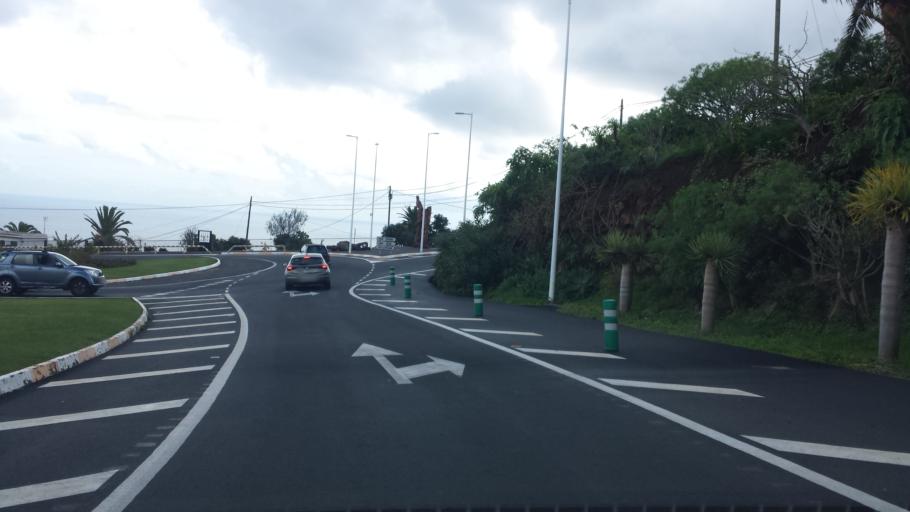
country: ES
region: Canary Islands
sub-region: Provincia de Santa Cruz de Tenerife
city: Brena Alta
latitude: 28.6612
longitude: -17.7814
